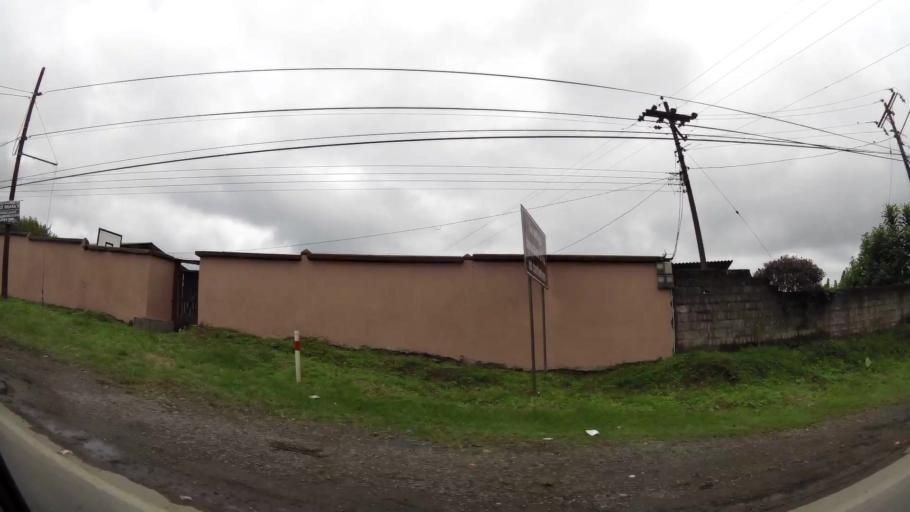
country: EC
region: Santo Domingo de los Tsachilas
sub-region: Canton Santo Domingo de los Colorados
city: Santo Domingo de los Colorados
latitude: -0.2692
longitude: -79.1110
